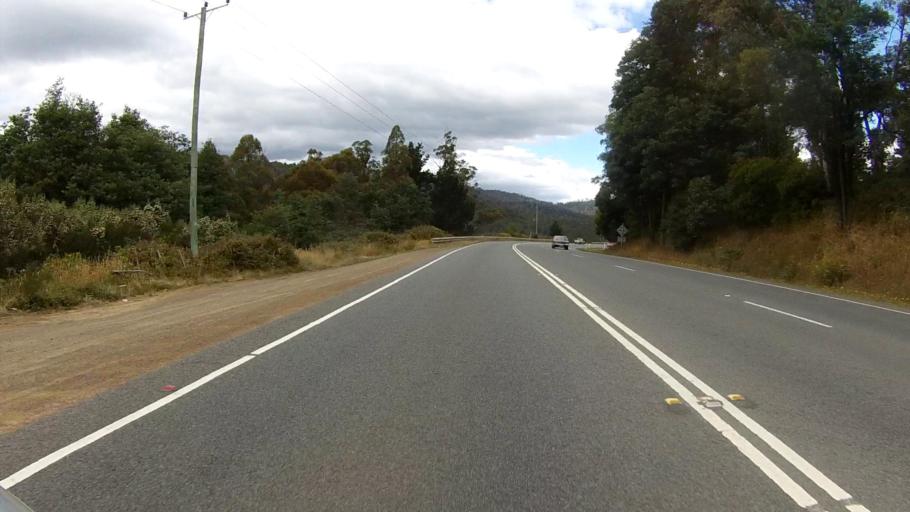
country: AU
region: Tasmania
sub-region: Huon Valley
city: Huonville
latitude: -42.9754
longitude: 147.1449
